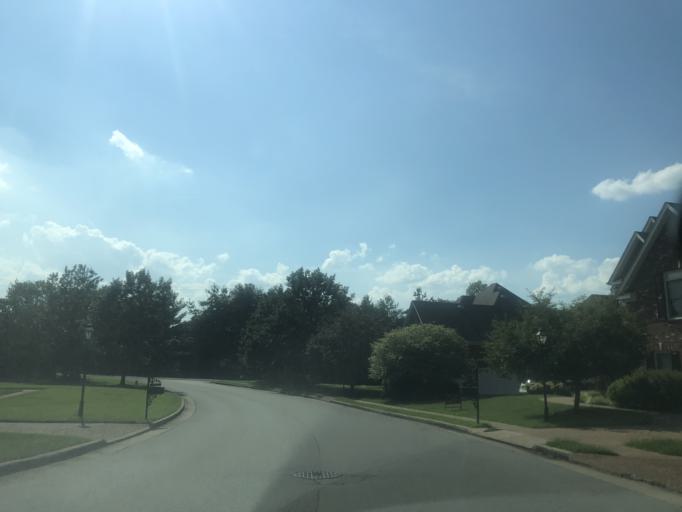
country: US
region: Tennessee
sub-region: Wilson County
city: Green Hill
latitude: 36.1510
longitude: -86.5830
